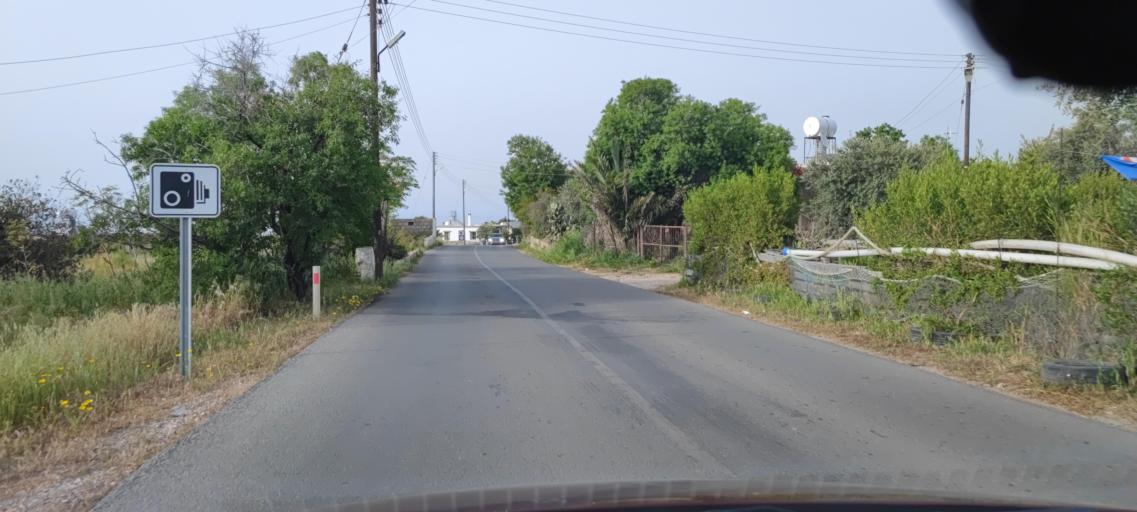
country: CY
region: Ammochostos
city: Leonarisso
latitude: 35.5390
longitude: 34.1936
